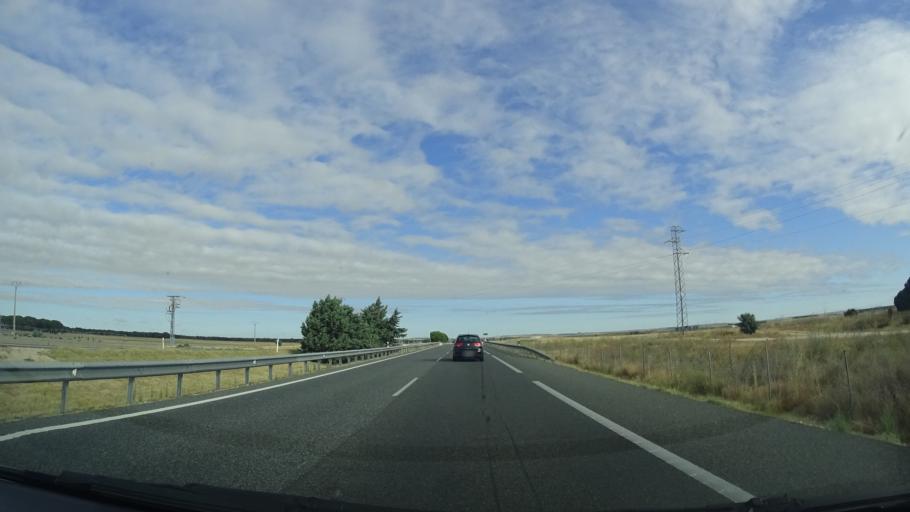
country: ES
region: Castille and Leon
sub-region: Provincia de Valladolid
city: San Vicente del Palacio
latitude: 41.2634
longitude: -4.8798
